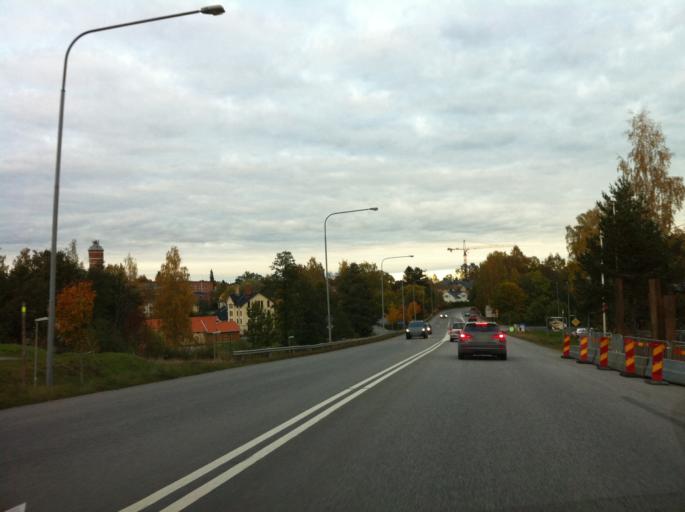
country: SE
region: OErebro
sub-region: Nora Kommun
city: Nora
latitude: 59.5001
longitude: 15.0349
